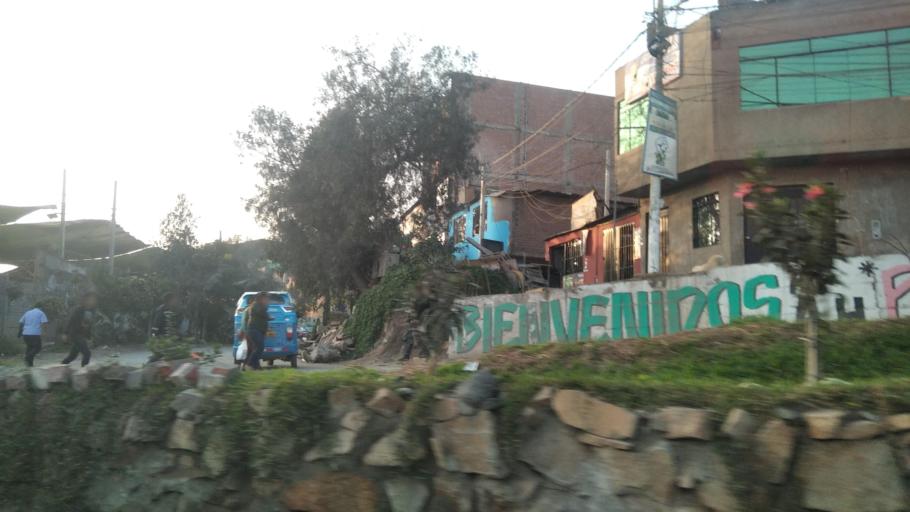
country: PE
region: Lima
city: Lima
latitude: -12.0127
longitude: -76.9946
